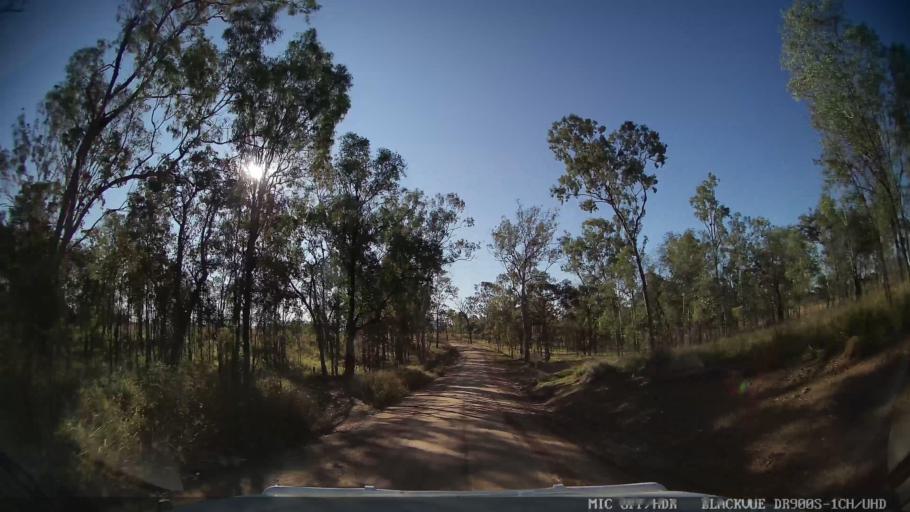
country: AU
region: Queensland
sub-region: Bundaberg
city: Sharon
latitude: -24.7888
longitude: 151.6074
